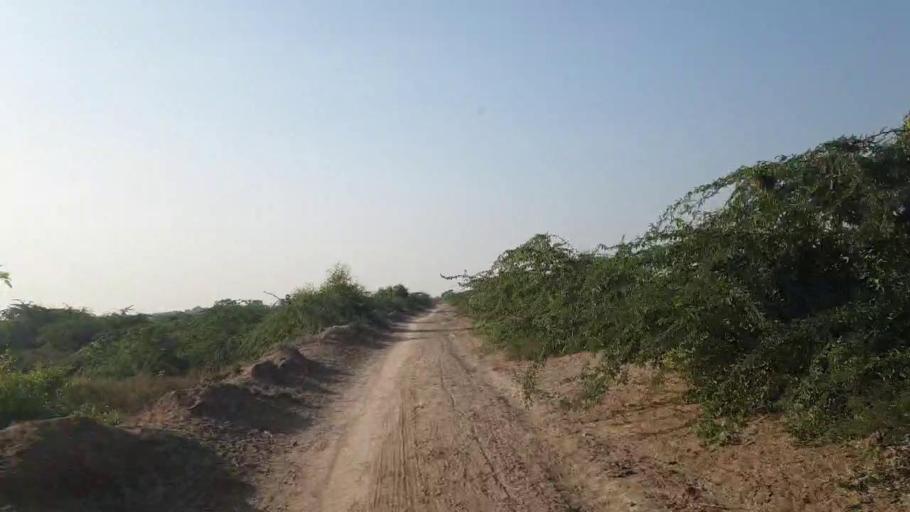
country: PK
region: Sindh
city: Badin
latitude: 24.4731
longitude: 68.7414
